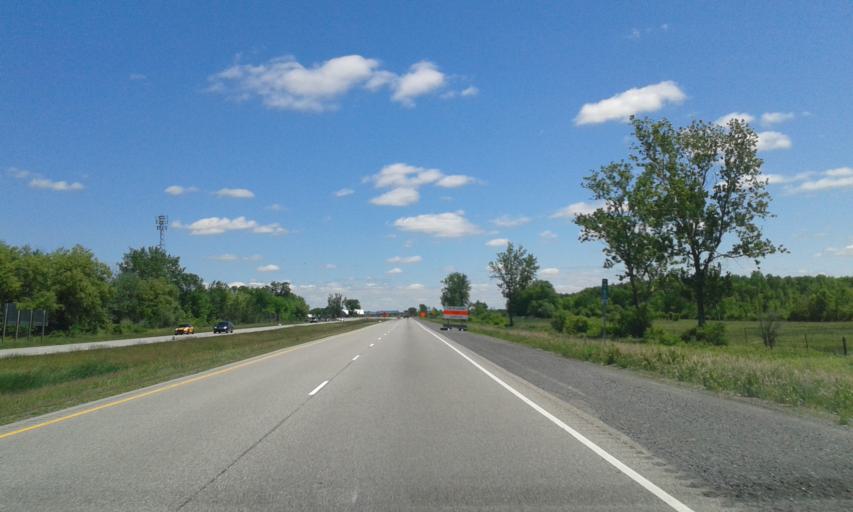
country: US
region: New York
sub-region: St. Lawrence County
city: Norfolk
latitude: 44.9604
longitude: -75.0915
